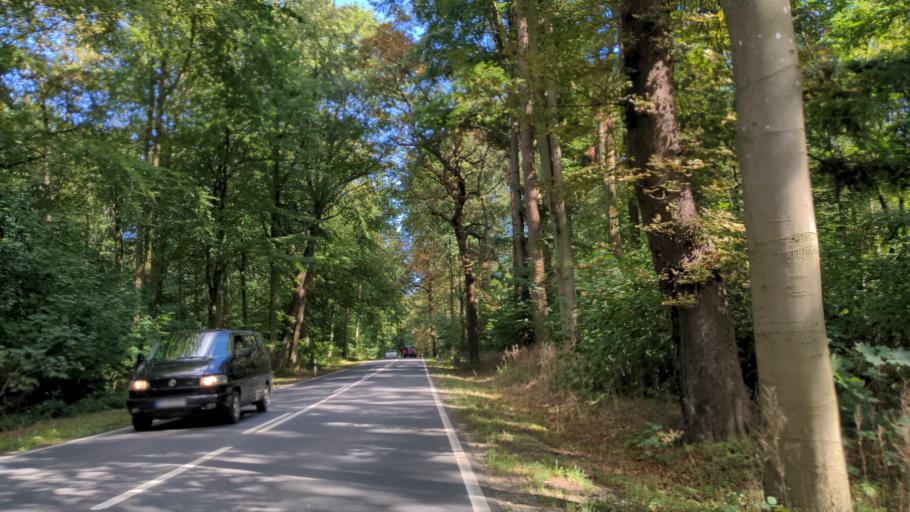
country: DE
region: Schleswig-Holstein
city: Kasseedorf
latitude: 54.1493
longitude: 10.7063
